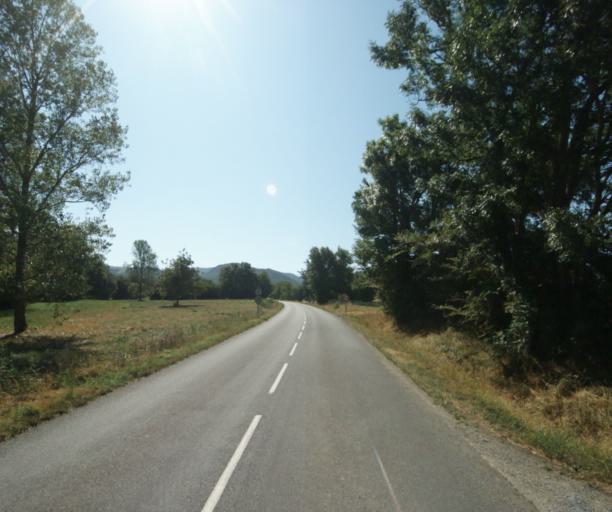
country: FR
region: Midi-Pyrenees
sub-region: Departement du Tarn
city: Soreze
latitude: 43.4595
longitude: 2.0435
